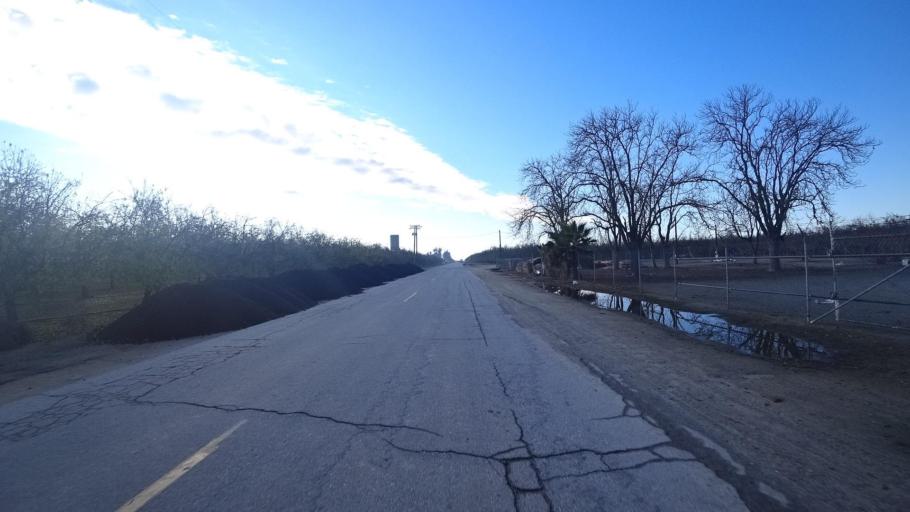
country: US
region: California
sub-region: Kern County
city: Delano
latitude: 35.7235
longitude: -119.3303
